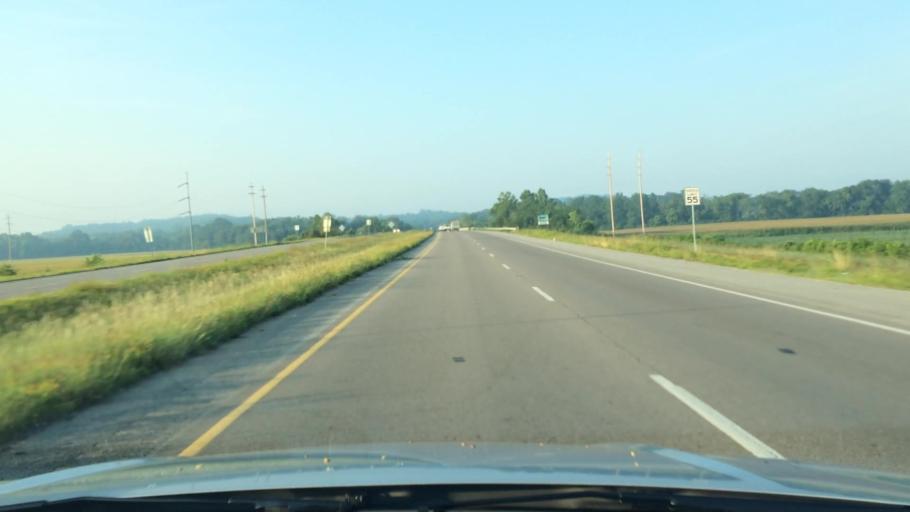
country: US
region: Tennessee
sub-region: Giles County
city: Pulaski
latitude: 35.2023
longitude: -87.0632
